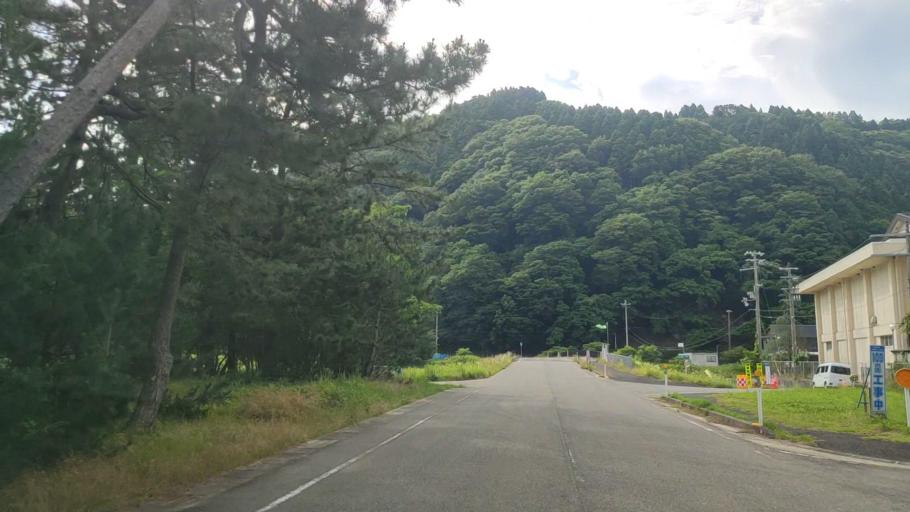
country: JP
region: Hyogo
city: Toyooka
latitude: 35.6416
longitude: 134.8392
